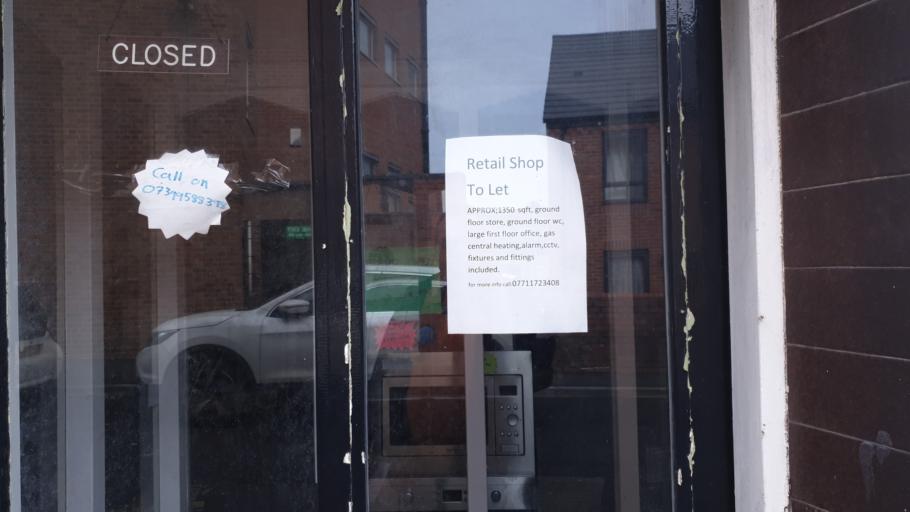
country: GB
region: England
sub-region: Telford and Wrekin
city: Wellington
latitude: 52.7023
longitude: -2.5192
